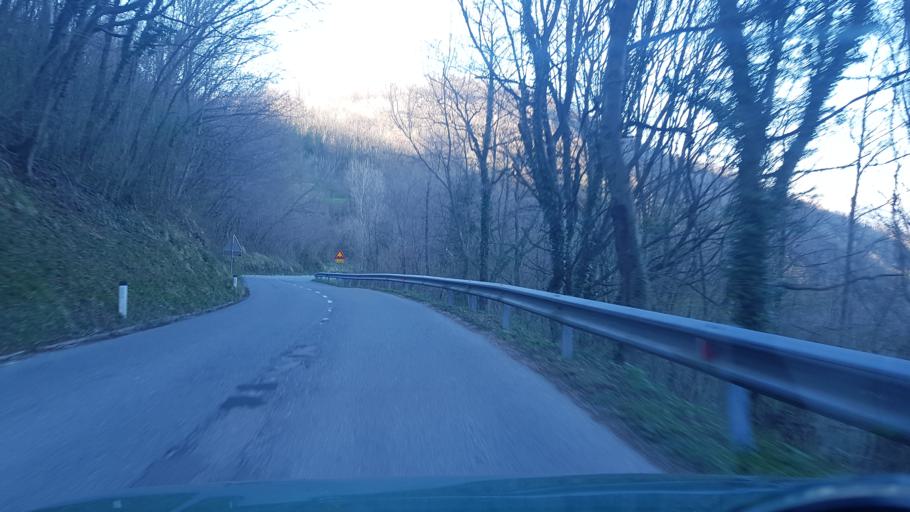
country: IT
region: Friuli Venezia Giulia
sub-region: Provincia di Gorizia
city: San Floriano del Collio
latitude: 46.0249
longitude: 13.5756
